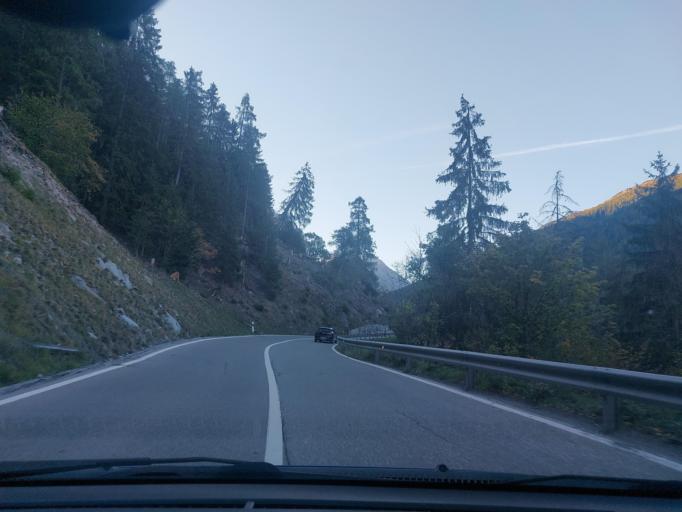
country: CH
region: Valais
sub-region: Sierre District
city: Chippis
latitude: 46.2247
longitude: 7.5817
